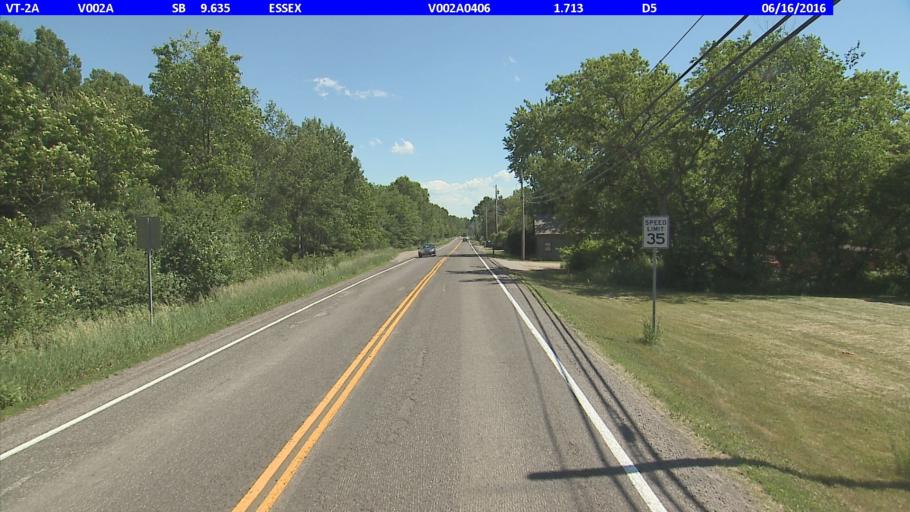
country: US
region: Vermont
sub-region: Chittenden County
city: Essex Junction
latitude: 44.5051
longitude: -73.1161
